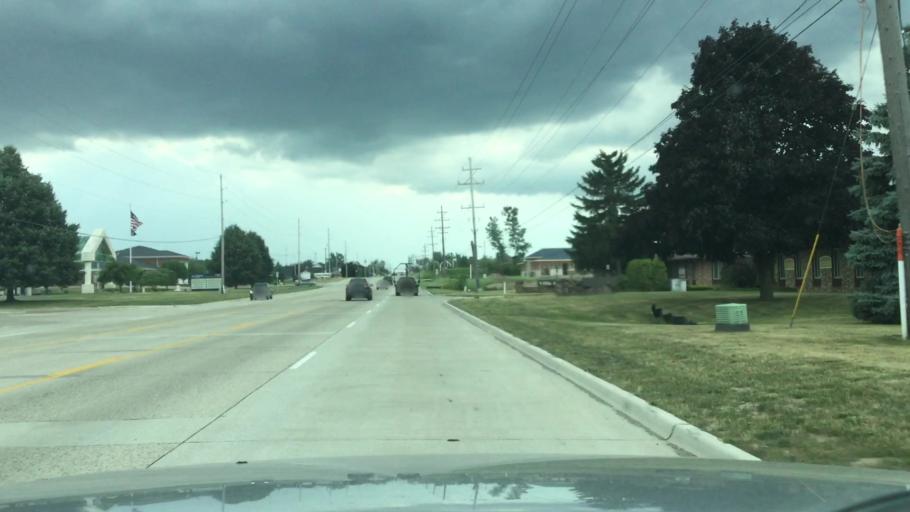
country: US
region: Michigan
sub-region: Genesee County
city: Swartz Creek
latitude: 43.0141
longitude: -83.7731
